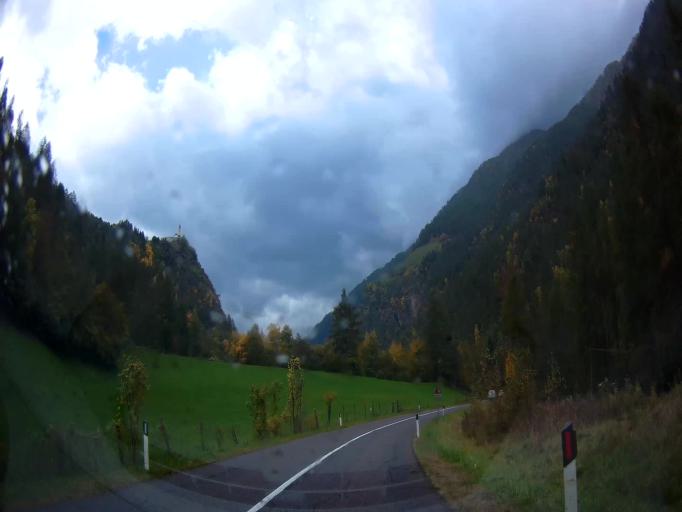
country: IT
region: Trentino-Alto Adige
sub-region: Bolzano
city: Certosa
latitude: 46.6932
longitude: 10.9279
